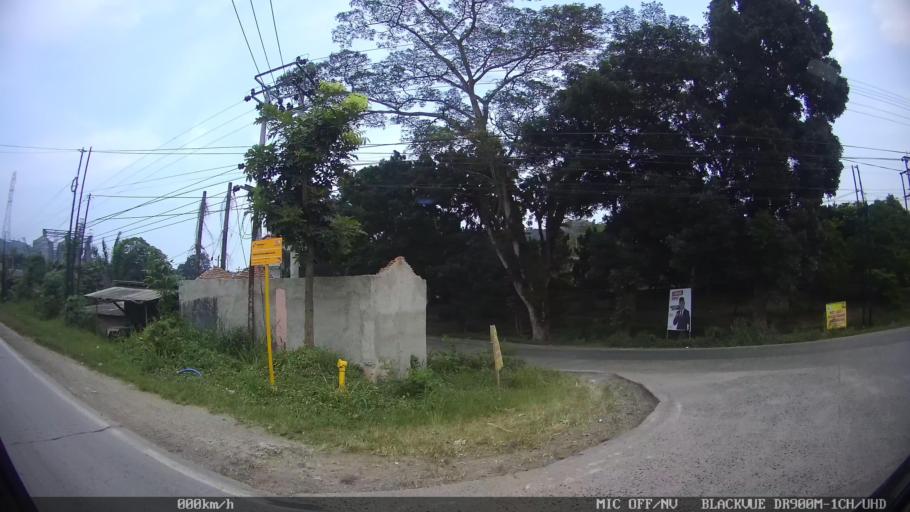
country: ID
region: Lampung
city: Panjang
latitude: -5.4199
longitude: 105.3372
